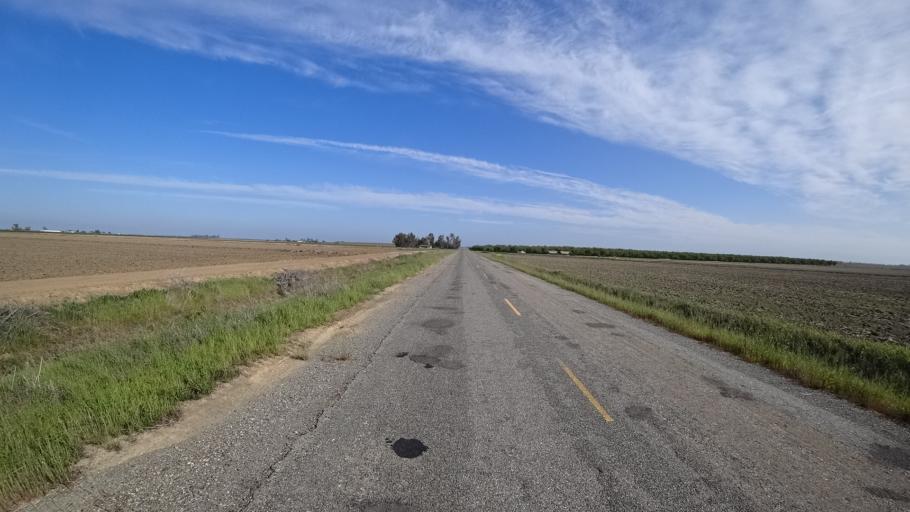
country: US
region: California
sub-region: Glenn County
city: Hamilton City
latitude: 39.6065
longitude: -122.0463
